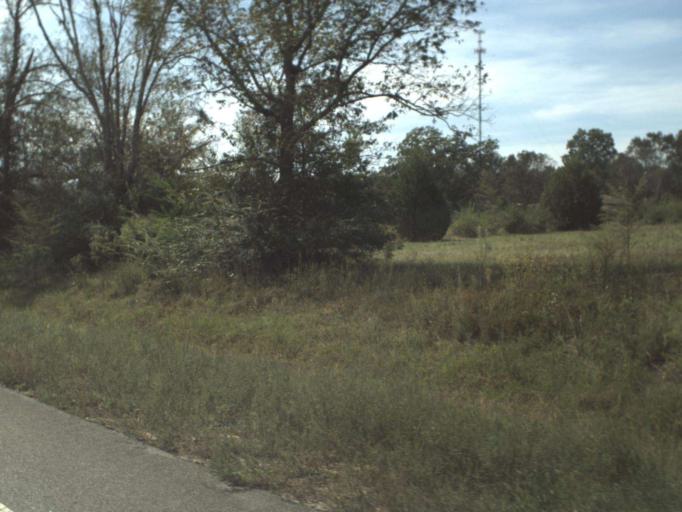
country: US
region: Florida
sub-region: Washington County
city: Chipley
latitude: 30.6546
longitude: -85.5805
